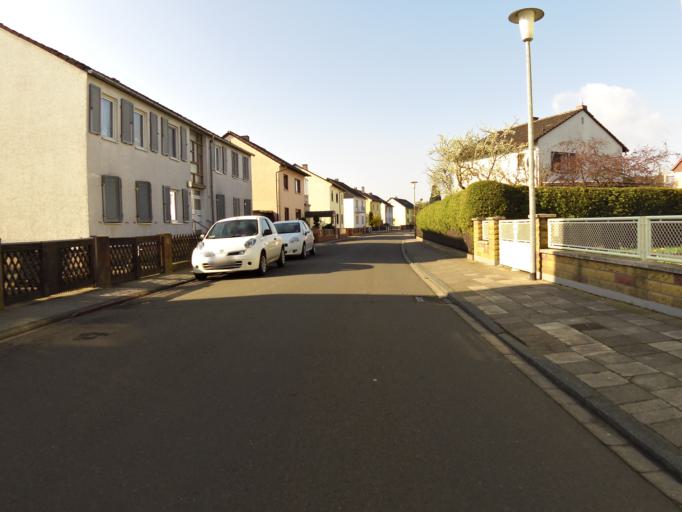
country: DE
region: Rheinland-Pfalz
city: Bobenheim-Roxheim
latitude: 49.5909
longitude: 8.3615
